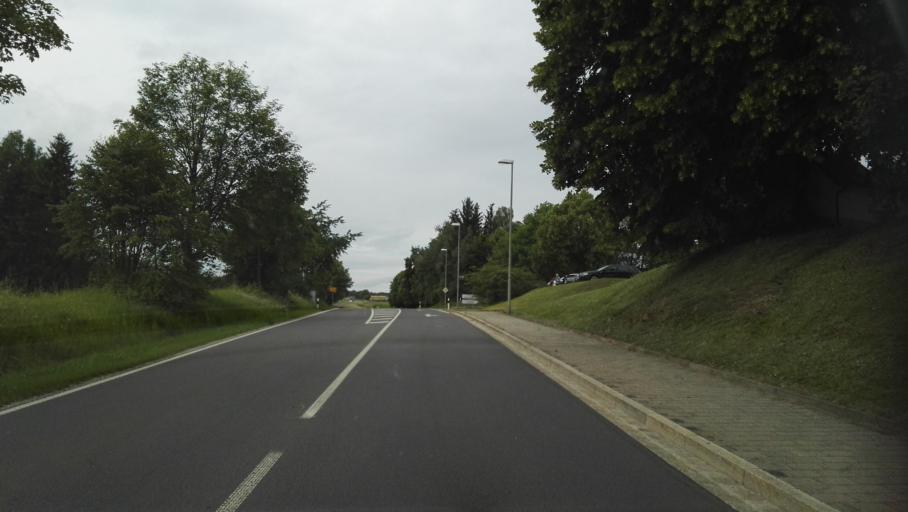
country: DE
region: Bavaria
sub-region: Upper Franconia
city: Hollfeld
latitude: 49.9422
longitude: 11.2881
